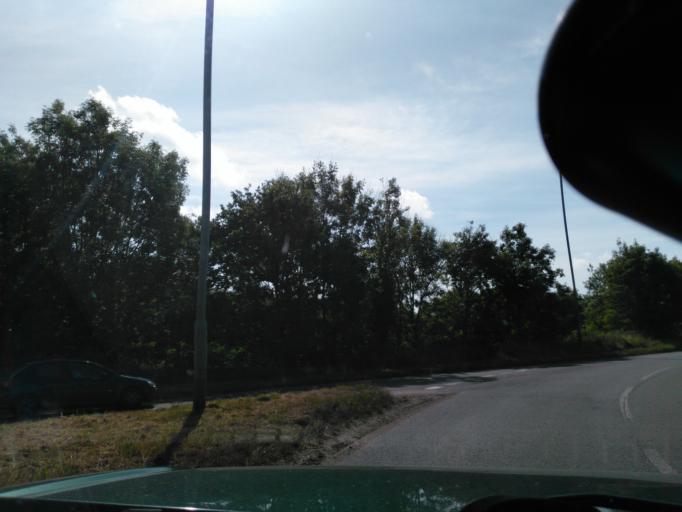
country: GB
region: England
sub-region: Hampshire
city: Romsey
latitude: 50.9542
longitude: -1.5343
